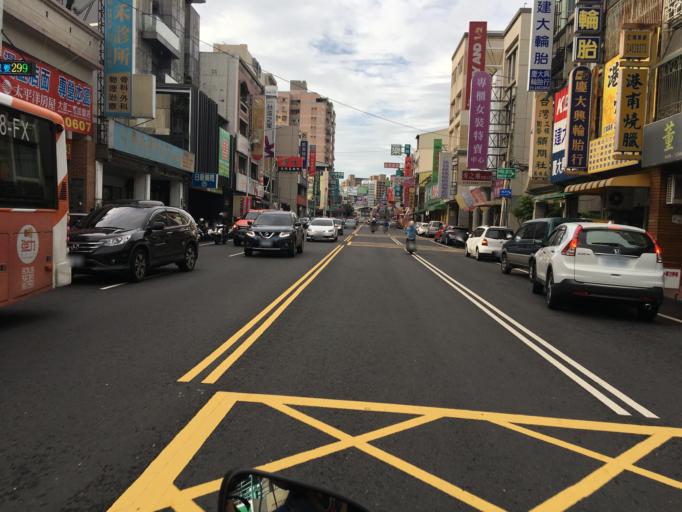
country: TW
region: Taiwan
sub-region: Taichung City
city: Taichung
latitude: 24.1032
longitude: 120.6887
